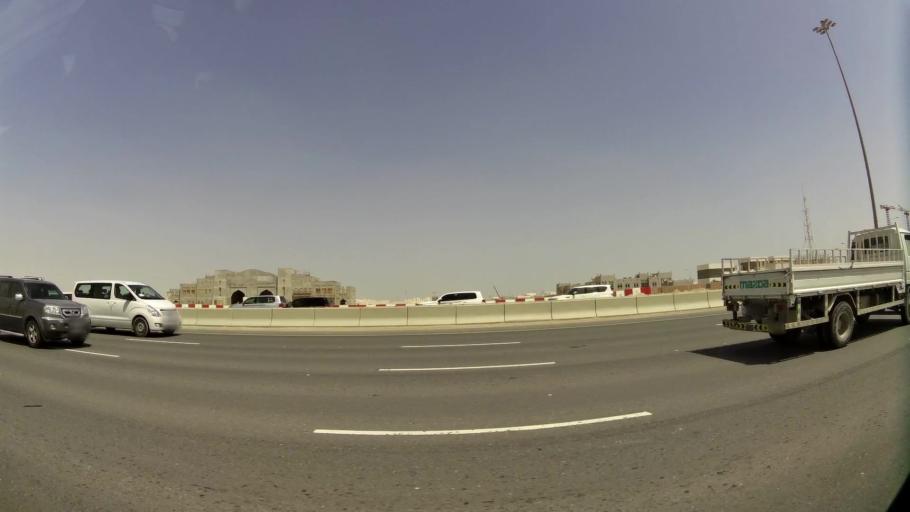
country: QA
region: Baladiyat ar Rayyan
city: Ar Rayyan
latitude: 25.3555
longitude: 51.4524
